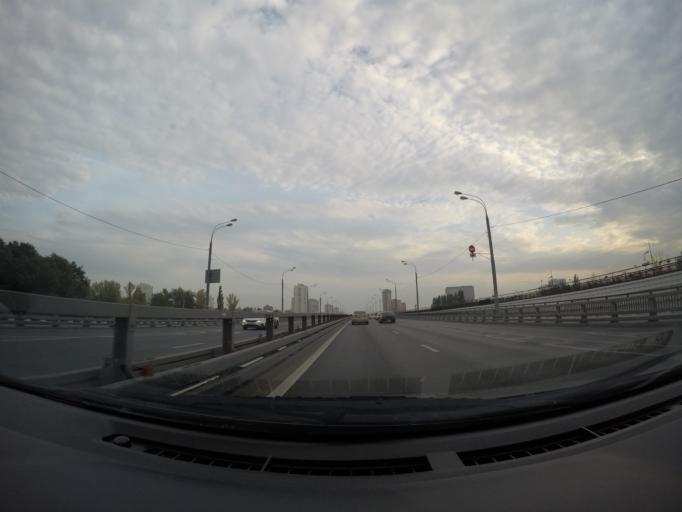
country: RU
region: Moskovskaya
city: Kozhukhovo
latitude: 55.6899
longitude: 37.6657
